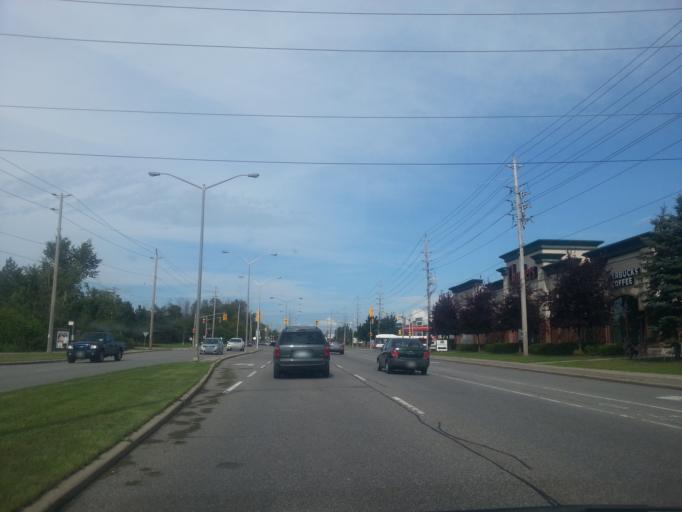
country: CA
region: Ontario
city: Ottawa
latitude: 45.4330
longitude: -75.6144
